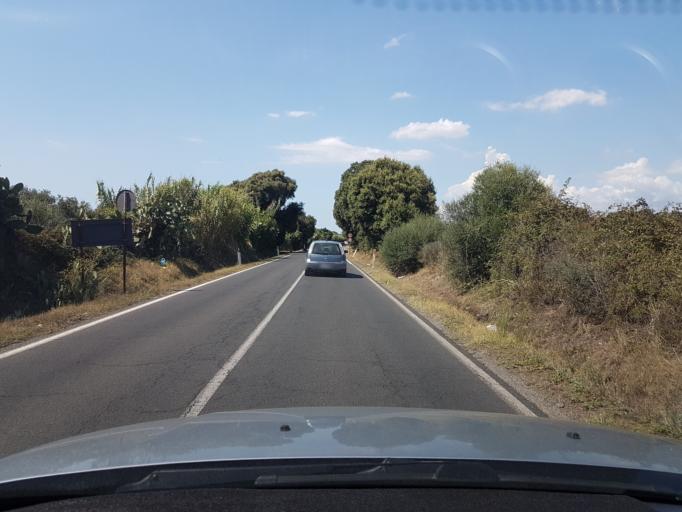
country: IT
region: Sardinia
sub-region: Provincia di Oristano
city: Donigala Fenugheddu
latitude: 39.9384
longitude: 8.5717
